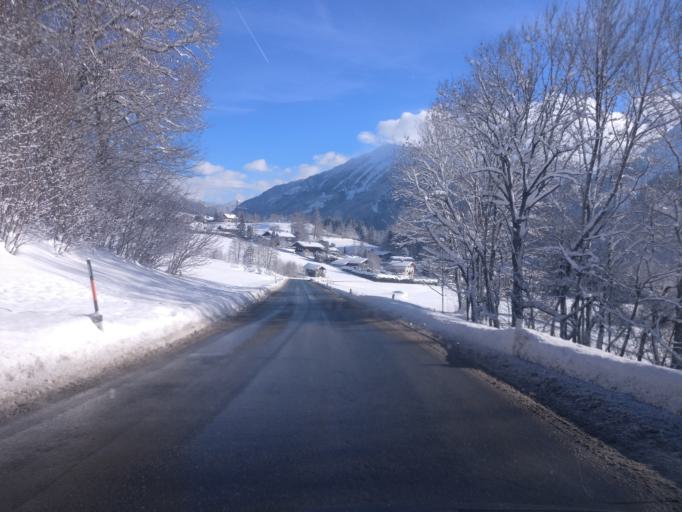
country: AT
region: Salzburg
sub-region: Politischer Bezirk Sankt Johann im Pongau
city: Goldegg
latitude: 47.3233
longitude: 13.0973
